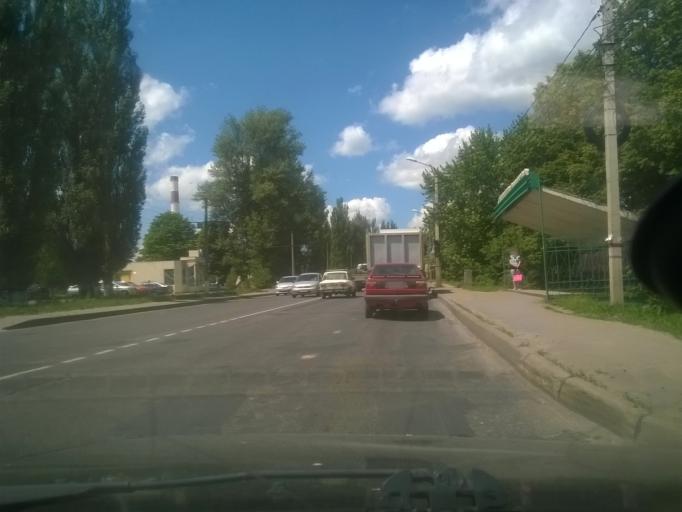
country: RU
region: Kursk
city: Kursk
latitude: 51.6617
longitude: 36.1254
